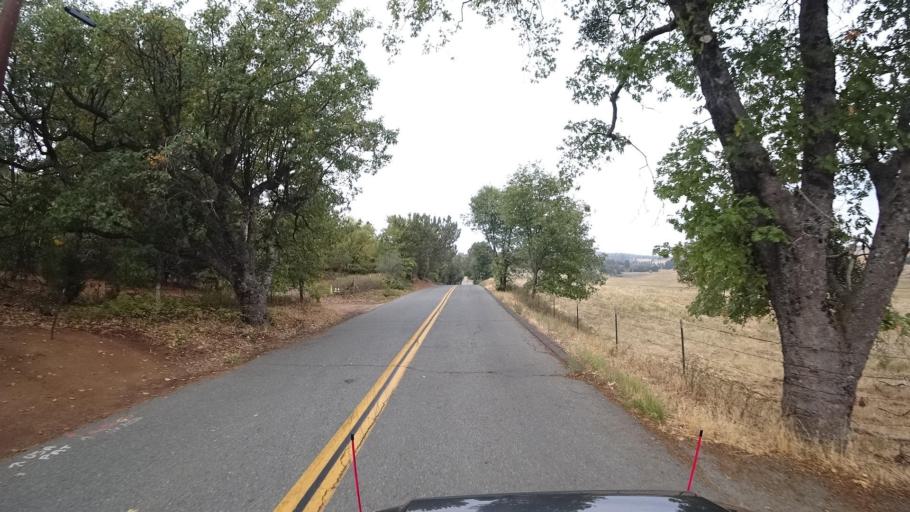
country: US
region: California
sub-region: San Diego County
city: Julian
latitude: 33.0426
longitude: -116.6012
